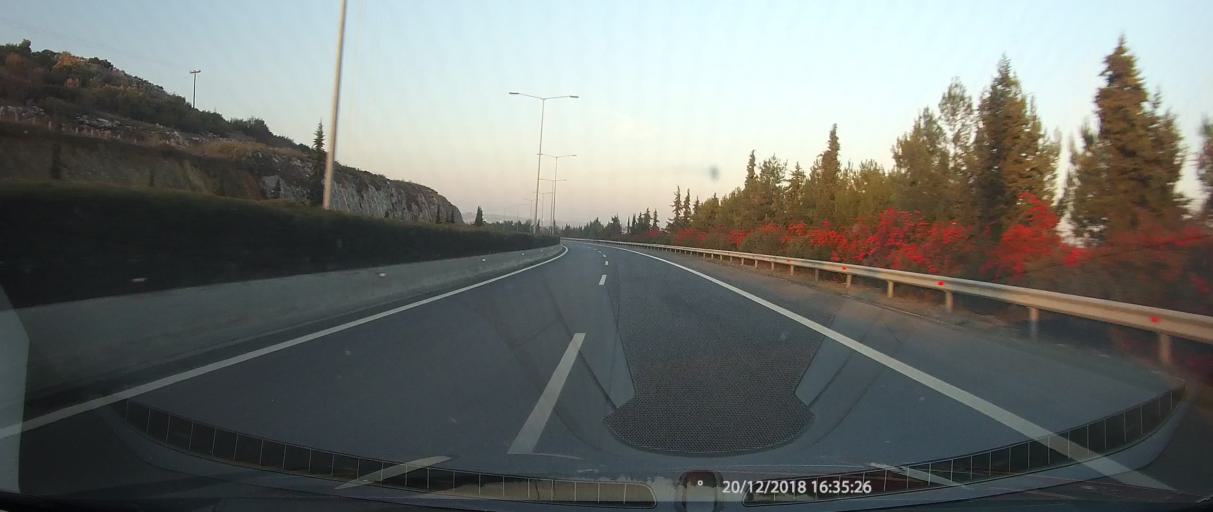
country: GR
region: Thessaly
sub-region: Nomos Magnisias
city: Nea Anchialos
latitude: 39.3030
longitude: 22.7484
